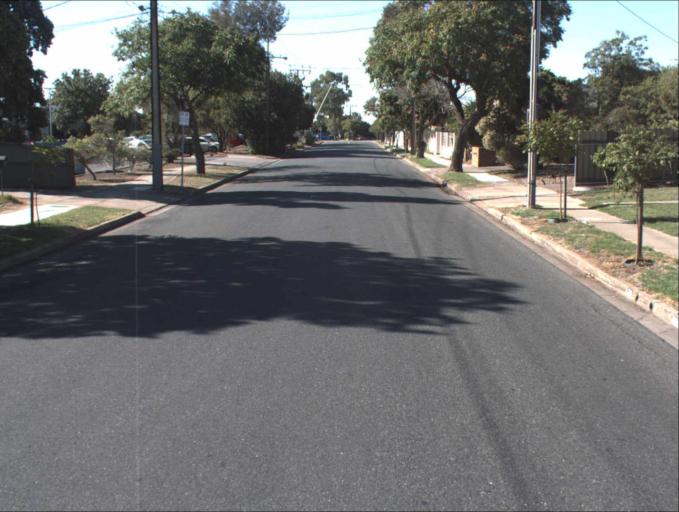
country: AU
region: South Australia
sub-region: Prospect
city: Prospect
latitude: -34.8769
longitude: 138.6039
